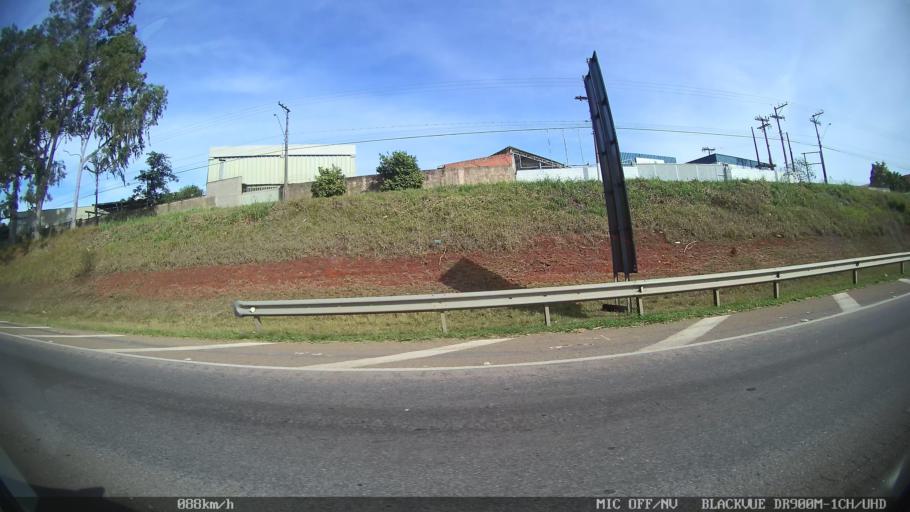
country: BR
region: Sao Paulo
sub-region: Piracicaba
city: Piracicaba
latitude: -22.7670
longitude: -47.5950
